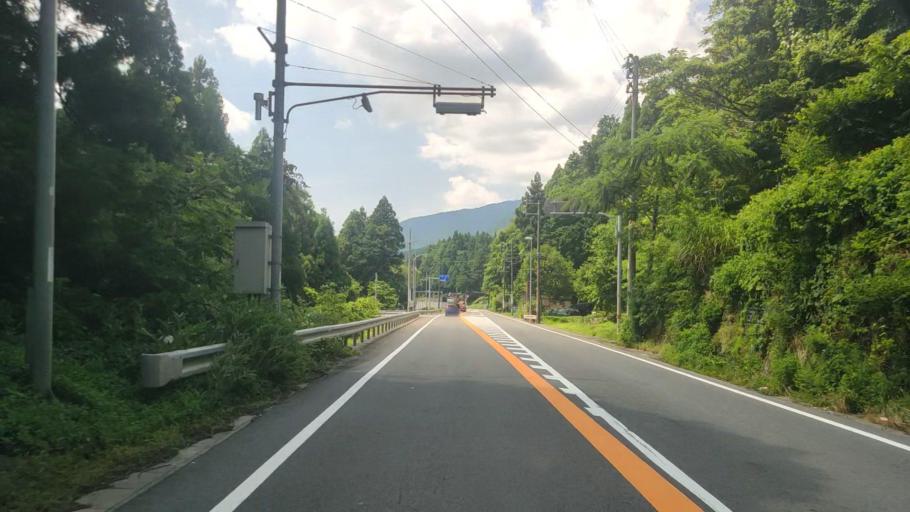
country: JP
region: Gifu
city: Tarui
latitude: 35.3788
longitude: 136.4390
